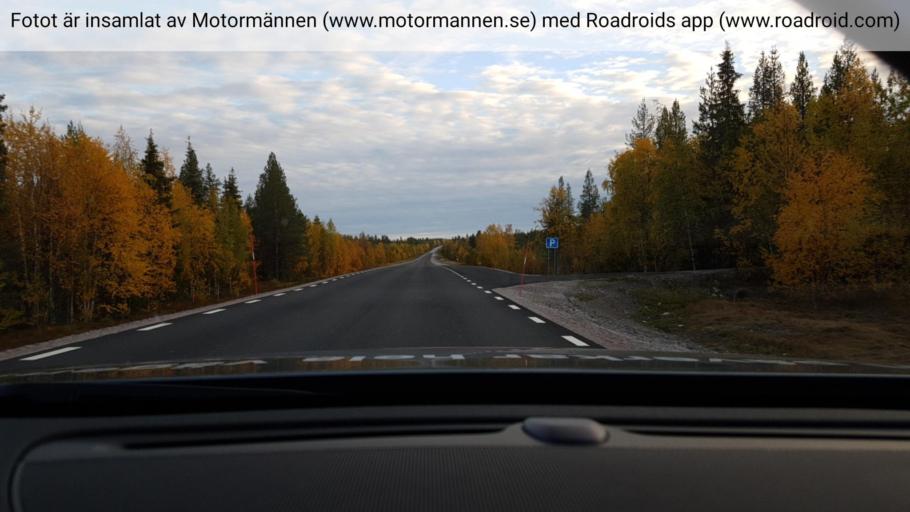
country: SE
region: Norrbotten
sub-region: Jokkmokks Kommun
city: Jokkmokk
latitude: 66.4518
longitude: 19.6944
